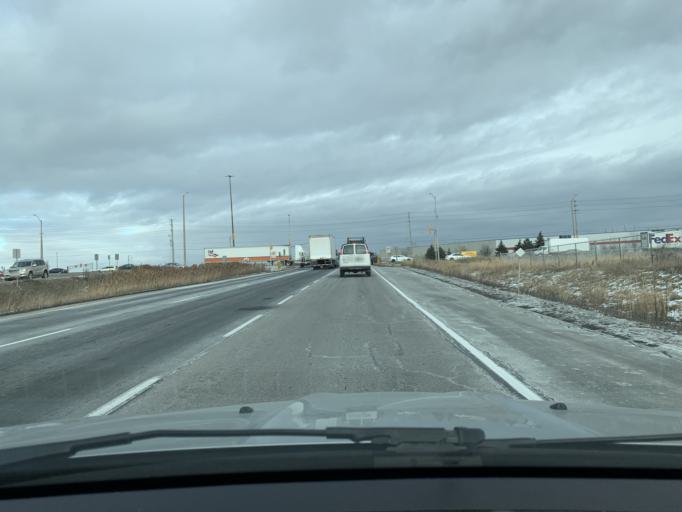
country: CA
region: Ontario
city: Brampton
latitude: 43.7250
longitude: -79.6727
